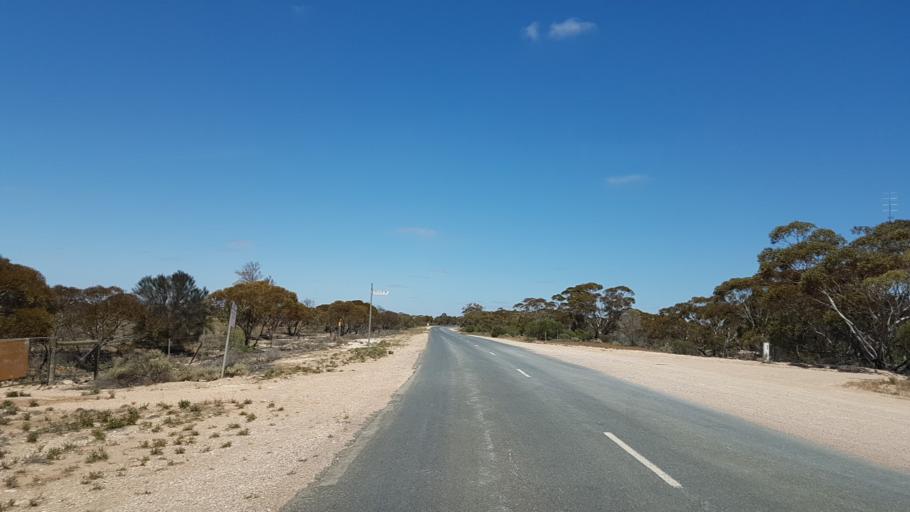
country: AU
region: South Australia
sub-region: Loxton Waikerie
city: Waikerie
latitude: -34.1837
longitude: 140.0217
